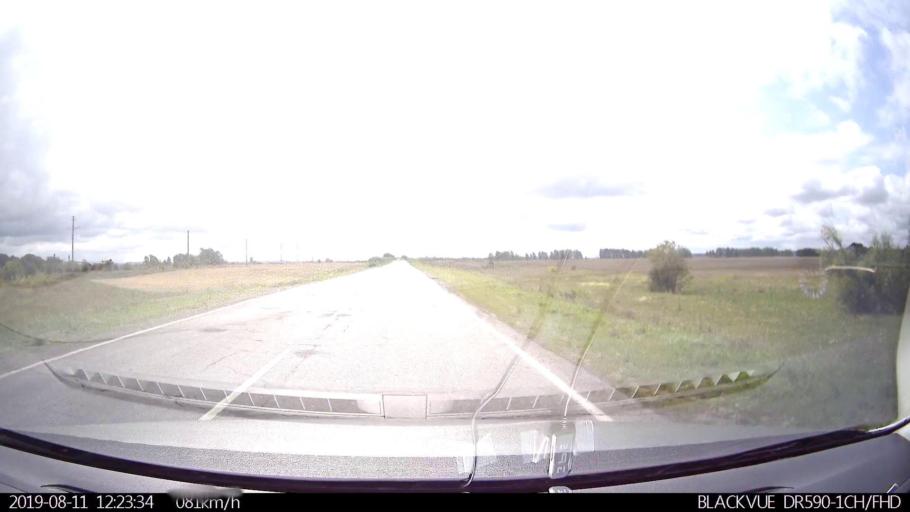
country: RU
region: Ulyanovsk
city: Ignatovka
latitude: 53.8938
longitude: 47.9503
